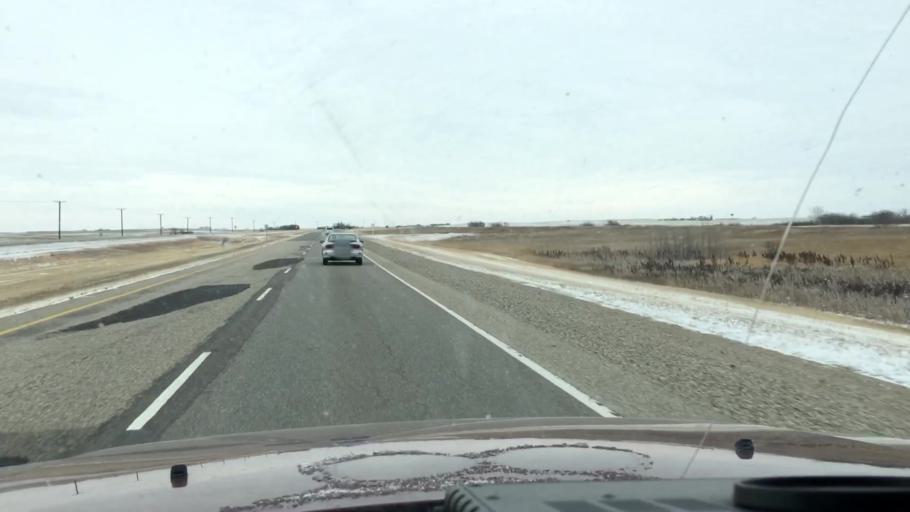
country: CA
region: Saskatchewan
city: Watrous
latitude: 51.4409
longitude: -106.2094
